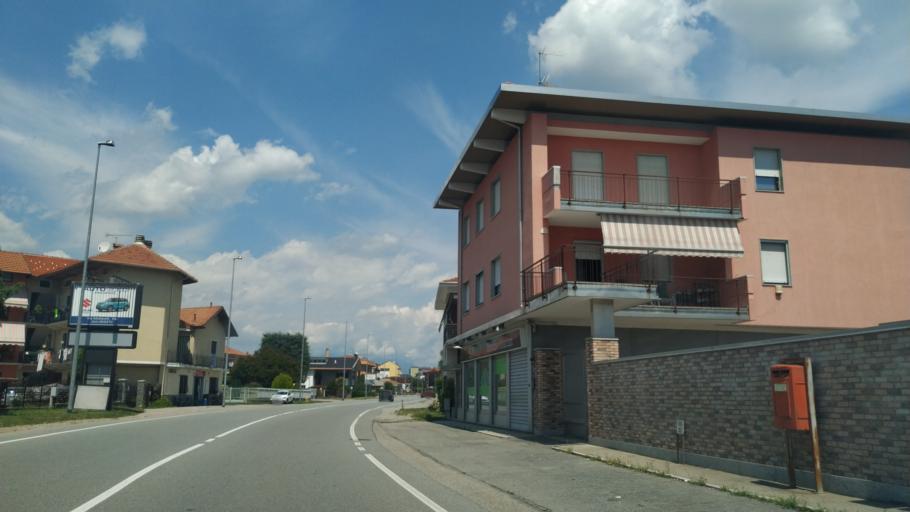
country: IT
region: Piedmont
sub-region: Provincia di Novara
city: Borgomanero
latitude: 45.7094
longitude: 8.4536
